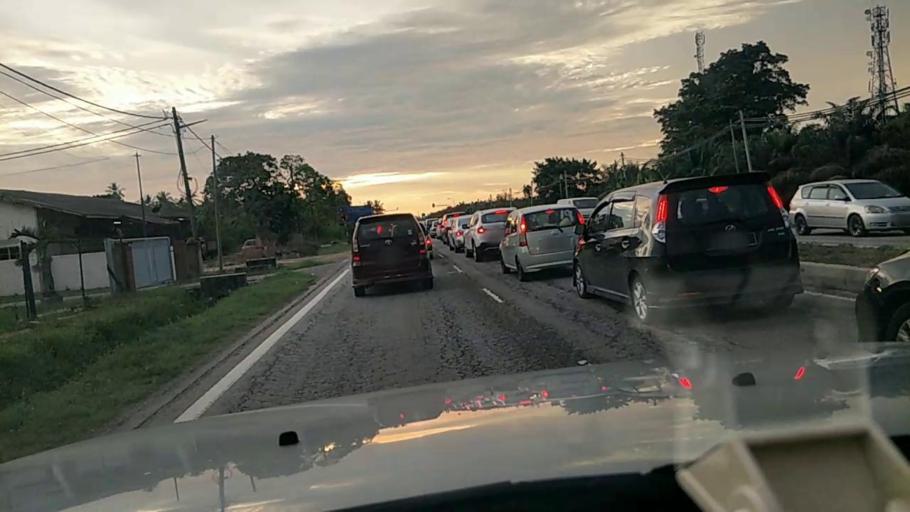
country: MY
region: Perak
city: Kampong Dungun
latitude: 3.1457
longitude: 101.3511
